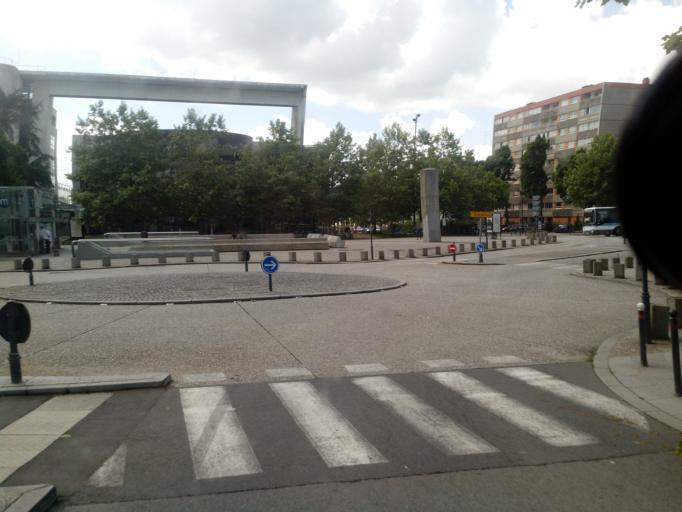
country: FR
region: Brittany
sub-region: Departement d'Ille-et-Vilaine
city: Rennes
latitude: 48.1217
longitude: -1.7038
